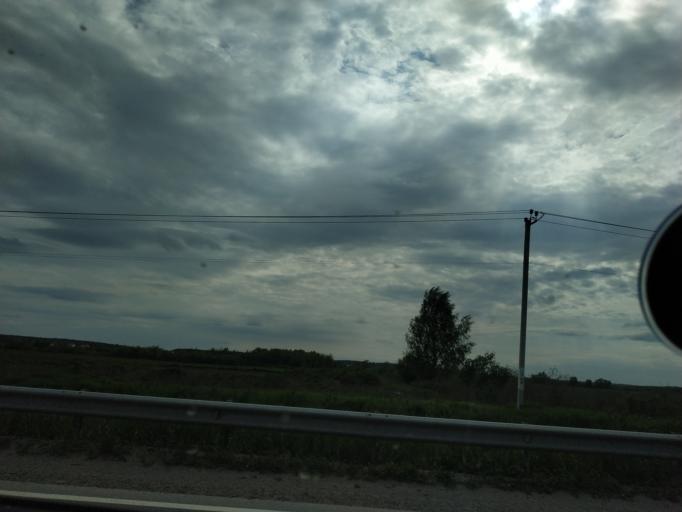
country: RU
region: Moskovskaya
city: Malyshevo
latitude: 55.4897
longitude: 38.3189
